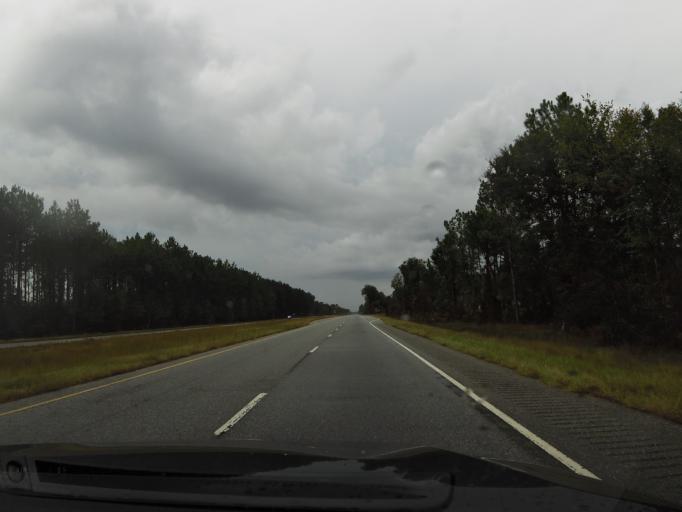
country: US
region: Georgia
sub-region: Wayne County
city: Jesup
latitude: 31.5238
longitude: -81.7819
